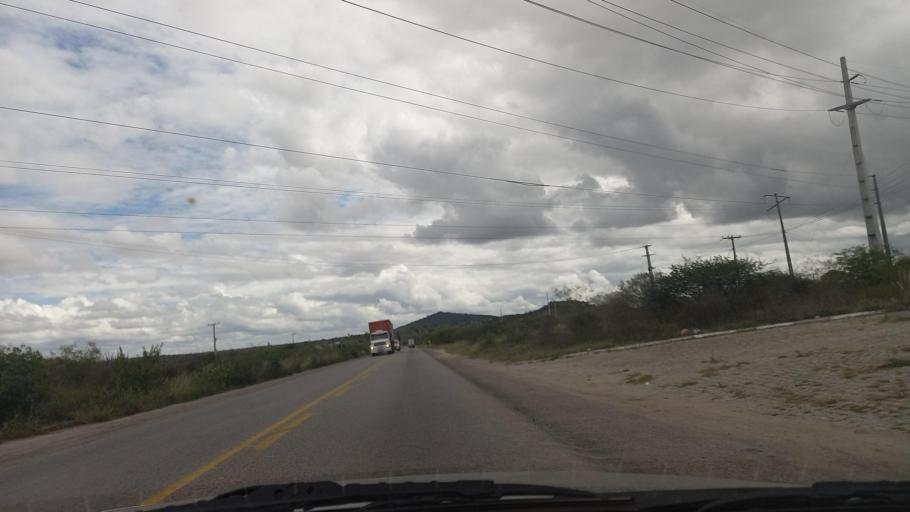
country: BR
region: Pernambuco
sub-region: Cachoeirinha
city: Cachoeirinha
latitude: -8.3350
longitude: -36.1537
